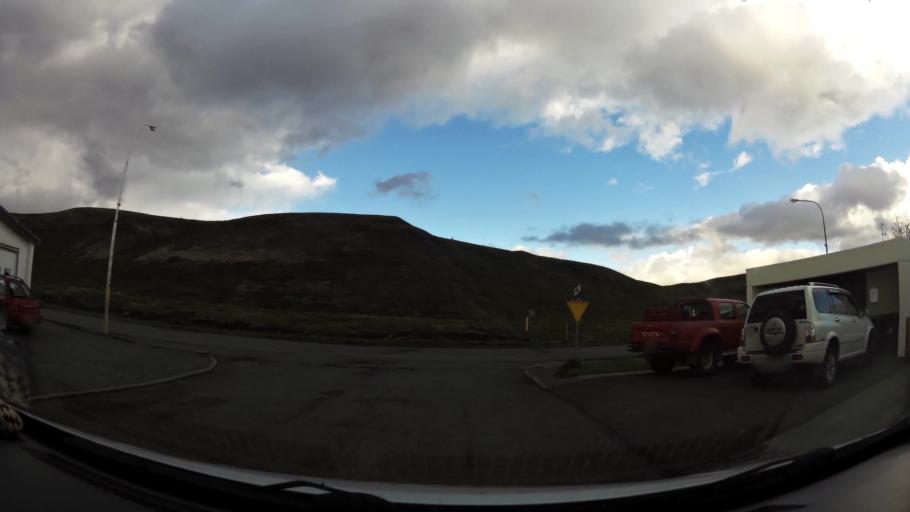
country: IS
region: Northeast
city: Laugar
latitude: 65.6421
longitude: -16.9022
